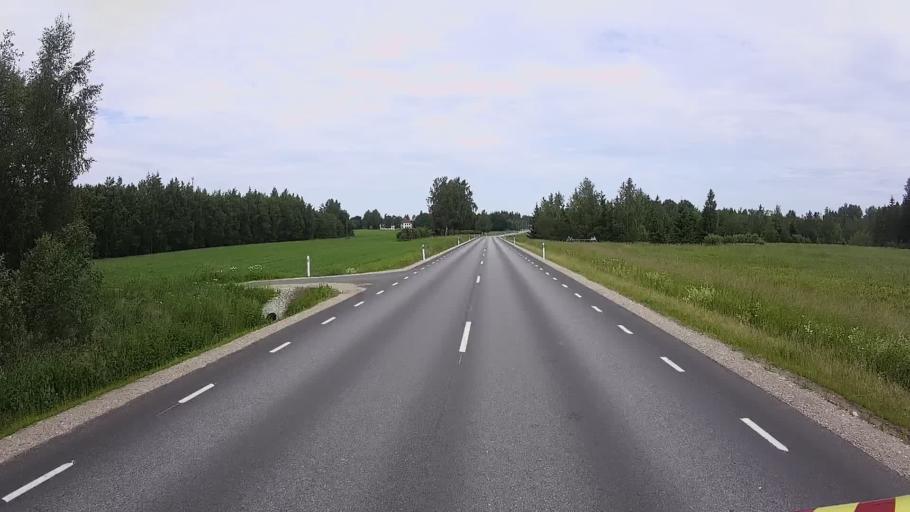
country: EE
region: Viljandimaa
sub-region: Viljandi linn
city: Viljandi
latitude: 58.2353
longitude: 25.5985
